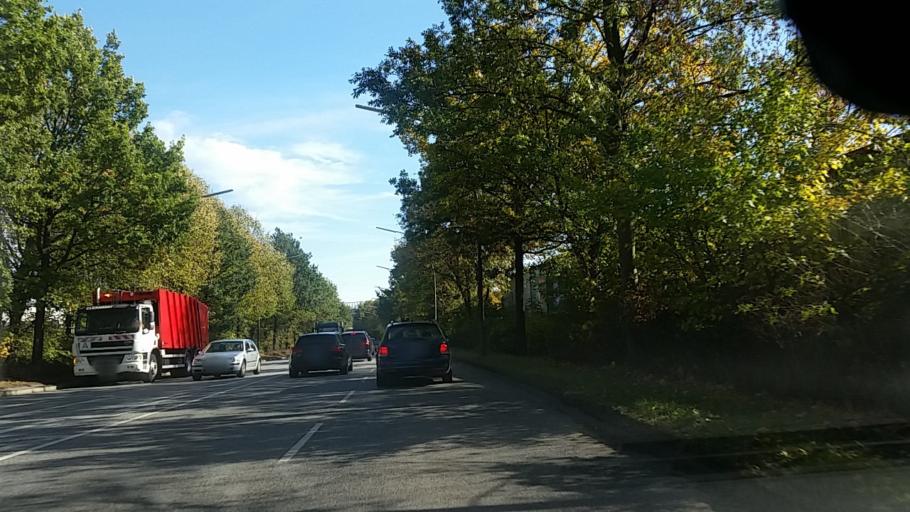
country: DE
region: Hamburg
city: Eidelstedt
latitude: 53.5914
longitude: 9.9091
